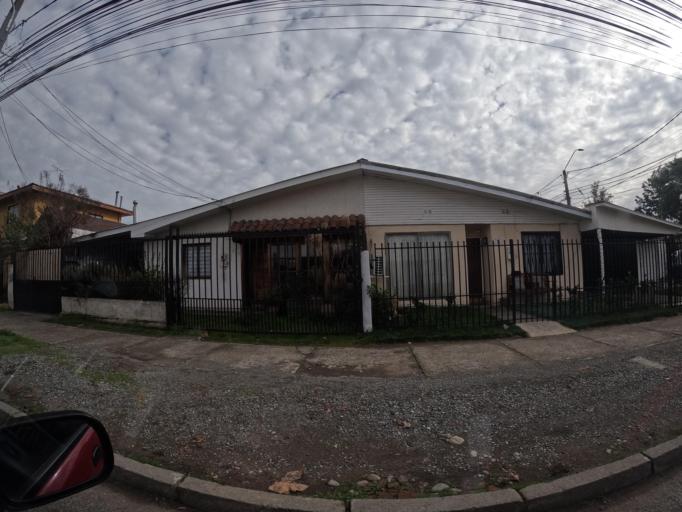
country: CL
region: Maule
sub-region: Provincia de Linares
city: Linares
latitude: -35.8411
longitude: -71.6037
